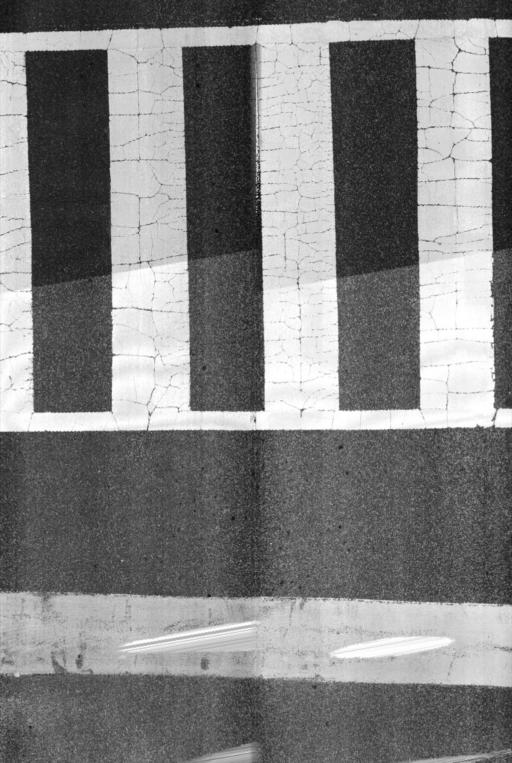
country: US
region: Maryland
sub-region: Prince George's County
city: Colmar Manor
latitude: 38.9229
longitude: -76.9549
